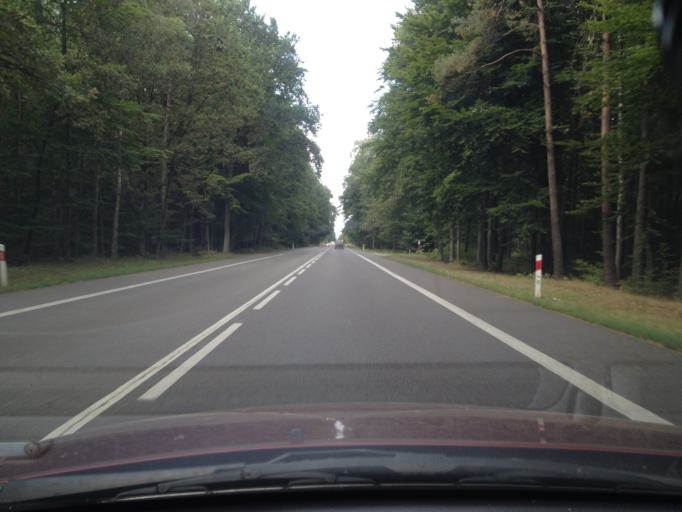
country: PL
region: West Pomeranian Voivodeship
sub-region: Powiat goleniowski
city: Przybiernow
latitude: 53.6876
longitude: 14.7977
